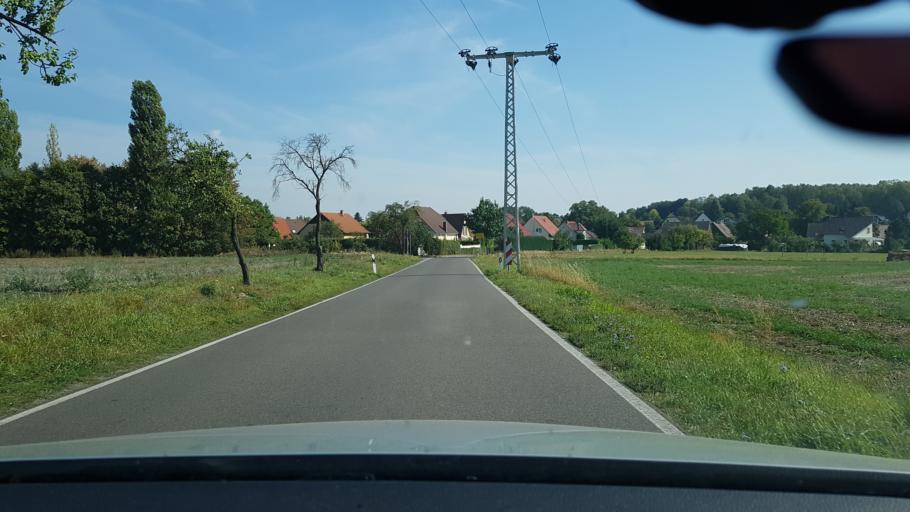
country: DE
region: Brandenburg
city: Lawitz
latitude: 52.1310
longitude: 14.5883
